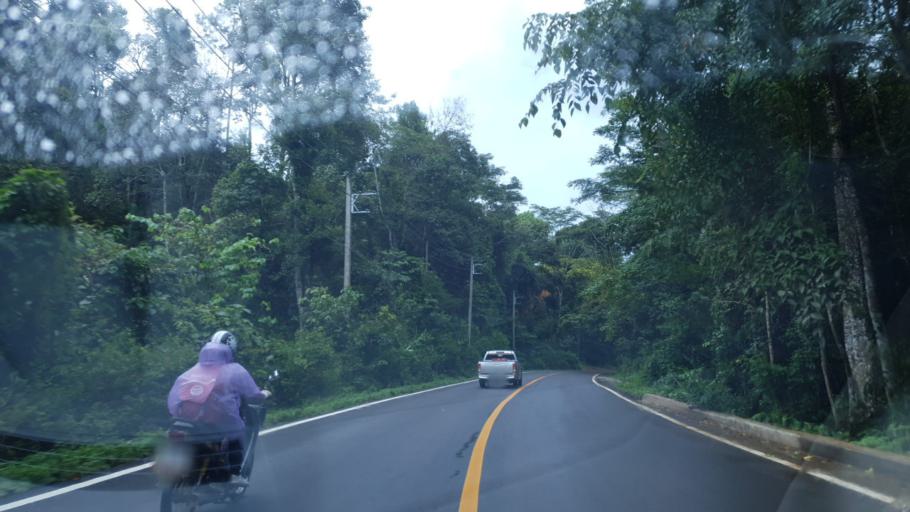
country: TH
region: Mae Hong Son
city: Ban Huai I Huak
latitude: 18.1501
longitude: 98.0953
